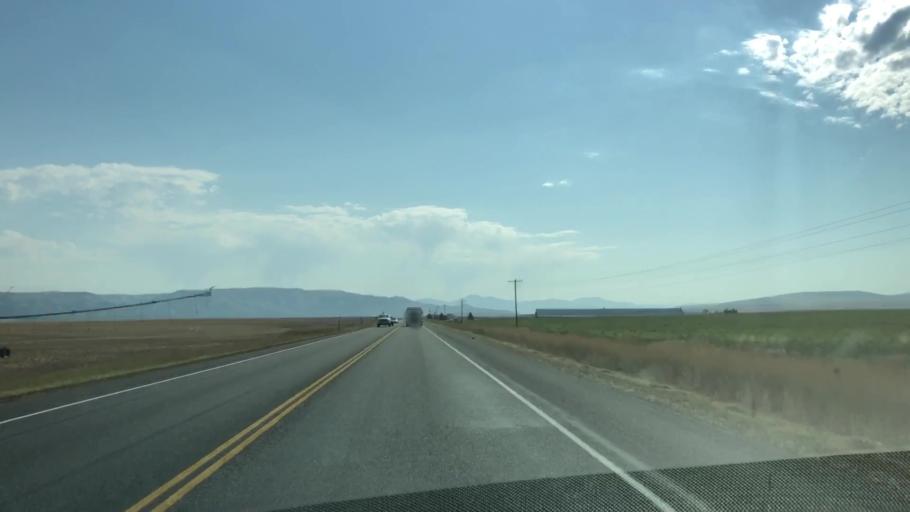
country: US
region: Idaho
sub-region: Jefferson County
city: Rigby
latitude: 43.6132
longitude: -111.7681
